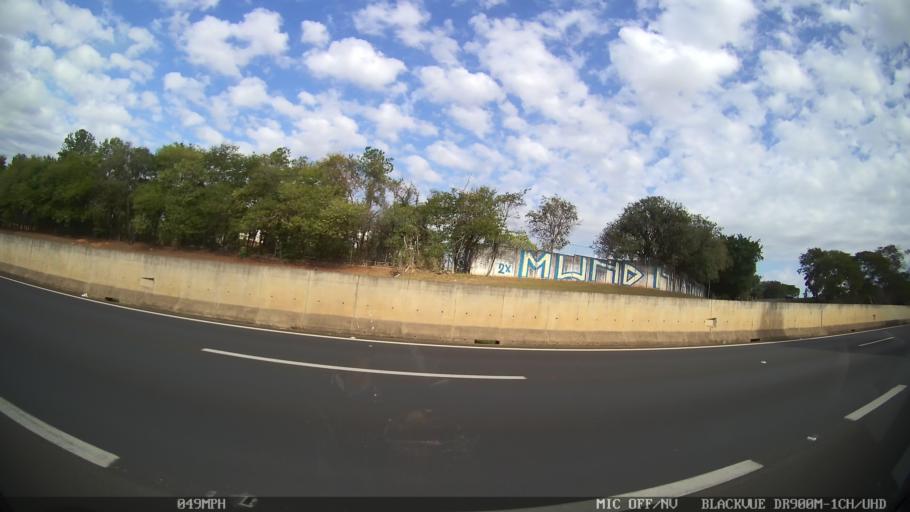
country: BR
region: Sao Paulo
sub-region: Limeira
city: Limeira
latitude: -22.5666
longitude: -47.4365
